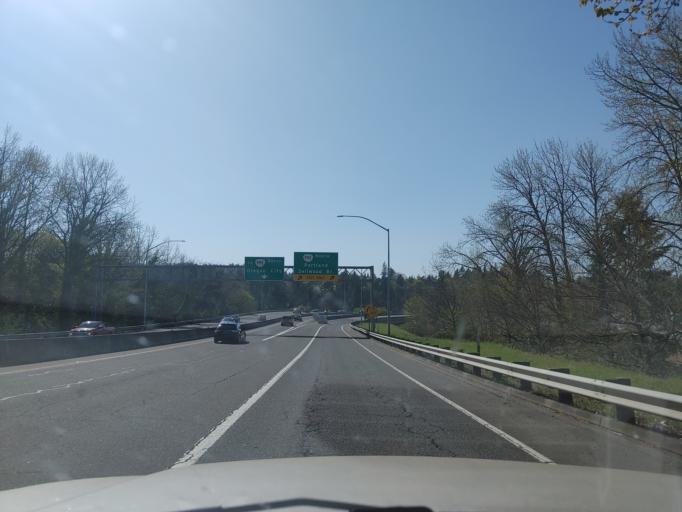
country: US
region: Oregon
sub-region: Clackamas County
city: Milwaukie
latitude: 45.4489
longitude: -122.6384
